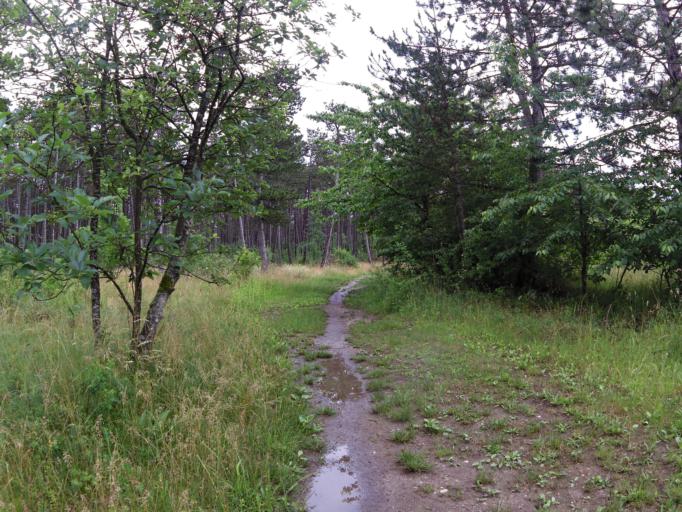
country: DE
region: Bavaria
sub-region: Regierungsbezirk Unterfranken
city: Erlabrunn
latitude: 49.8546
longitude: 9.8338
